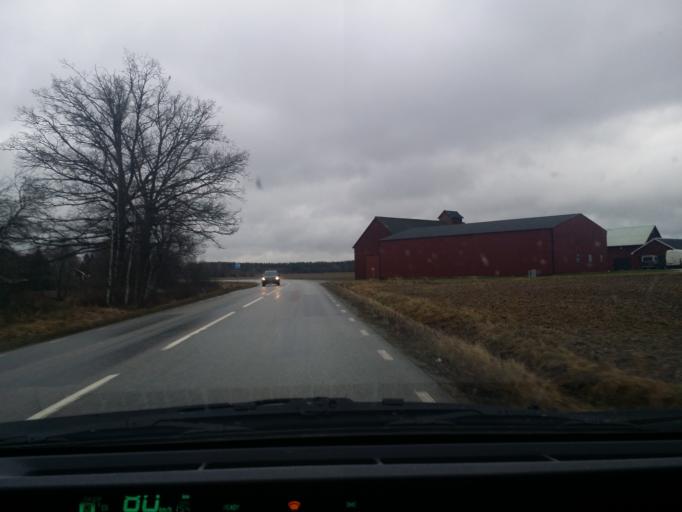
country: SE
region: Vaestmanland
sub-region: Vasteras
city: Skultuna
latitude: 59.8007
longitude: 16.5217
